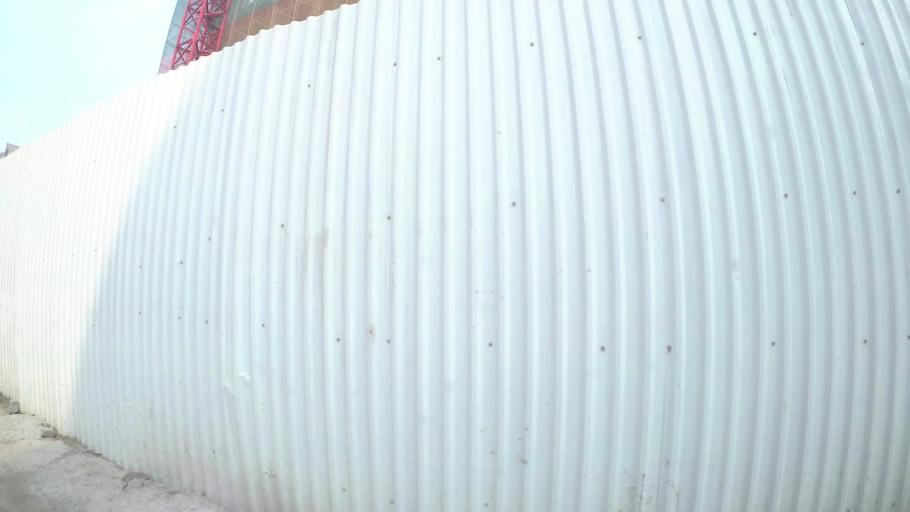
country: VN
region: Ha Noi
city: Thanh Xuan
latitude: 20.9850
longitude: 105.8009
